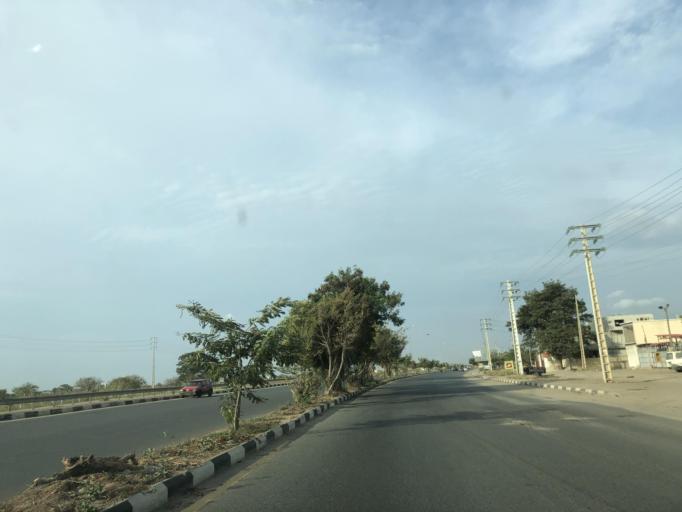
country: AO
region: Luanda
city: Luanda
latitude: -8.9385
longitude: 13.2958
